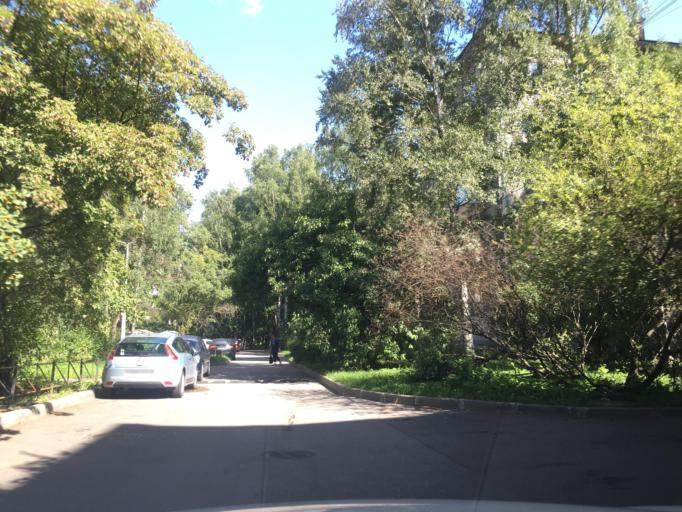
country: RU
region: Leningrad
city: Kalininskiy
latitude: 60.0028
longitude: 30.3949
